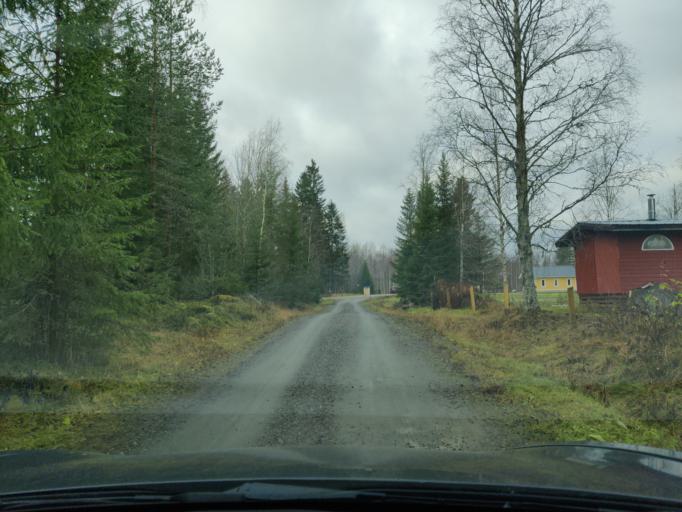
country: FI
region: Northern Savo
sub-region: Ylae-Savo
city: Kiuruvesi
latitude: 63.6413
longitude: 26.6333
